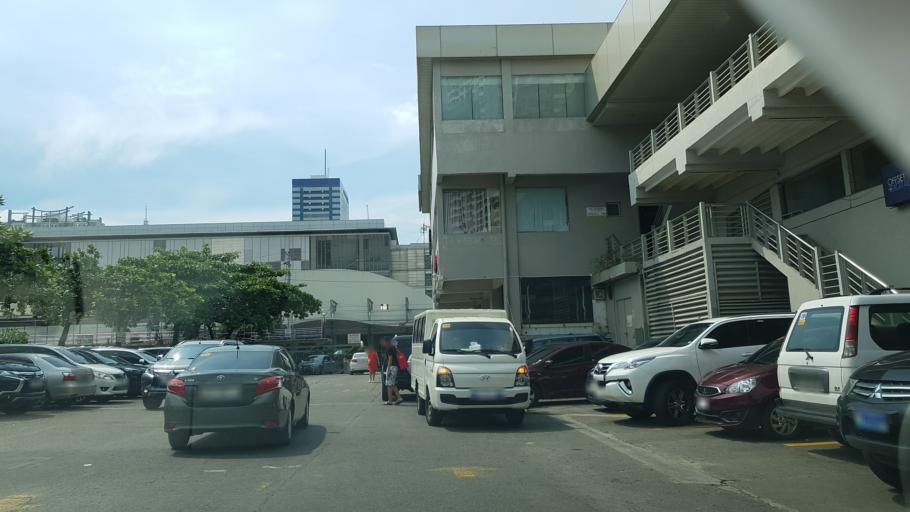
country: PH
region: Metro Manila
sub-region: Pasig
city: Pasig City
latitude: 14.5735
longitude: 121.0580
